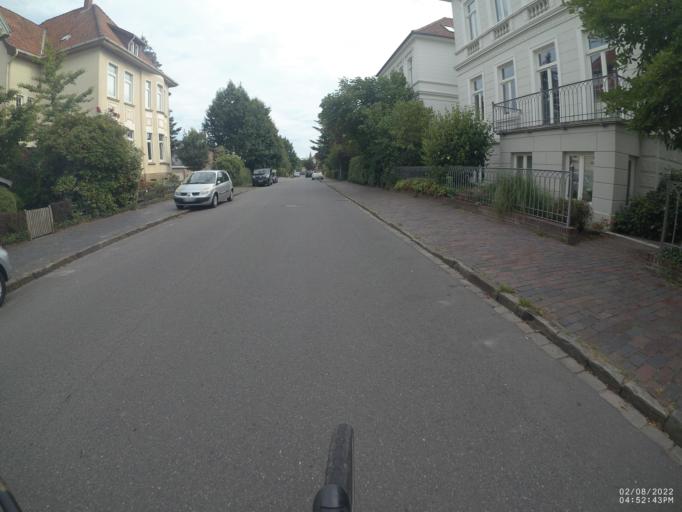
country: DE
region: Lower Saxony
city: Oldenburg
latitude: 53.1505
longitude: 8.2082
